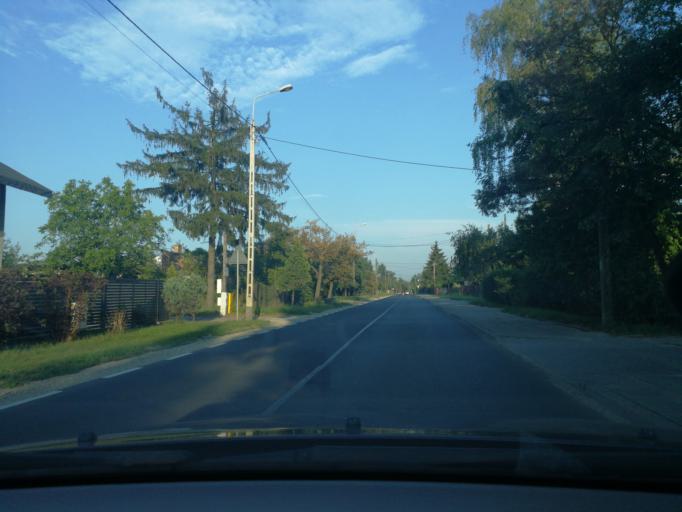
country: PL
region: Masovian Voivodeship
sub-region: Powiat warszawski zachodni
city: Ozarow Mazowiecki
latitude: 52.1895
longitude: 20.7570
